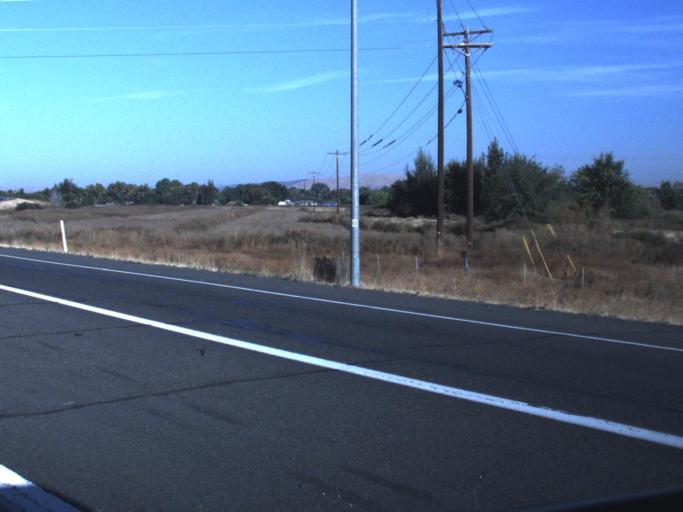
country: US
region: Washington
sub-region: Yakima County
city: Toppenish
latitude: 46.4155
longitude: -120.3092
